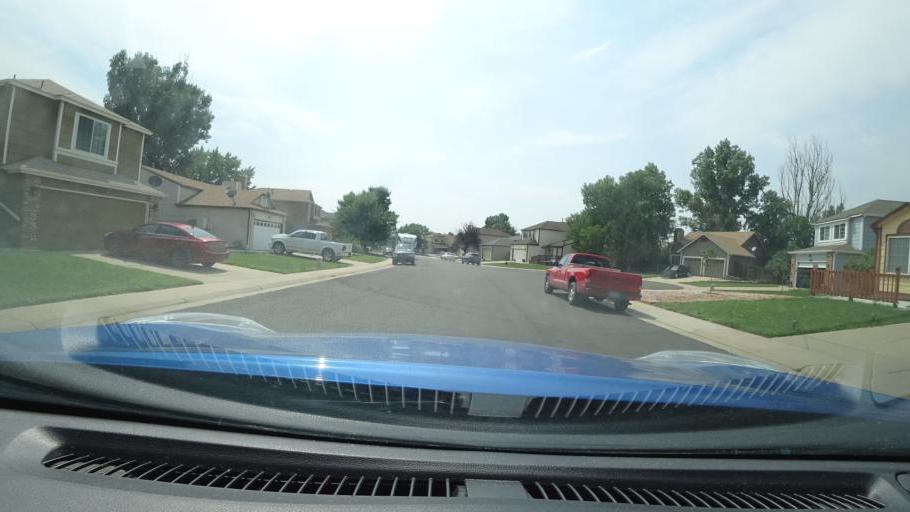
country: US
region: Colorado
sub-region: Adams County
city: Aurora
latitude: 39.7774
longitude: -104.7438
